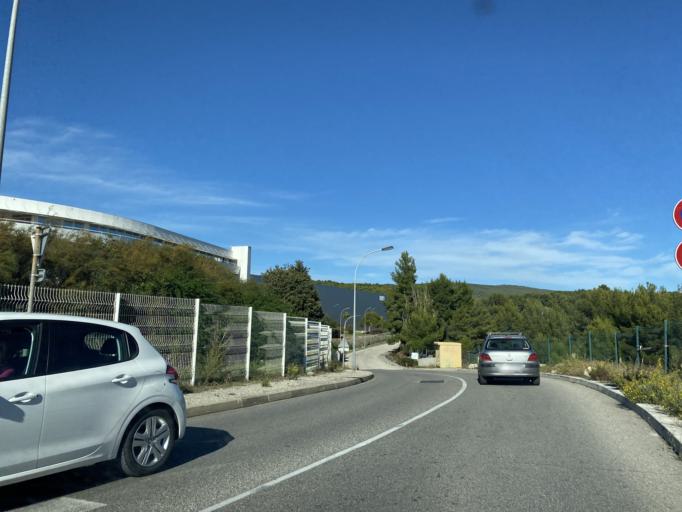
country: FR
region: Provence-Alpes-Cote d'Azur
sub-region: Departement des Bouches-du-Rhone
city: Ceyreste
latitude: 43.2068
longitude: 5.6019
